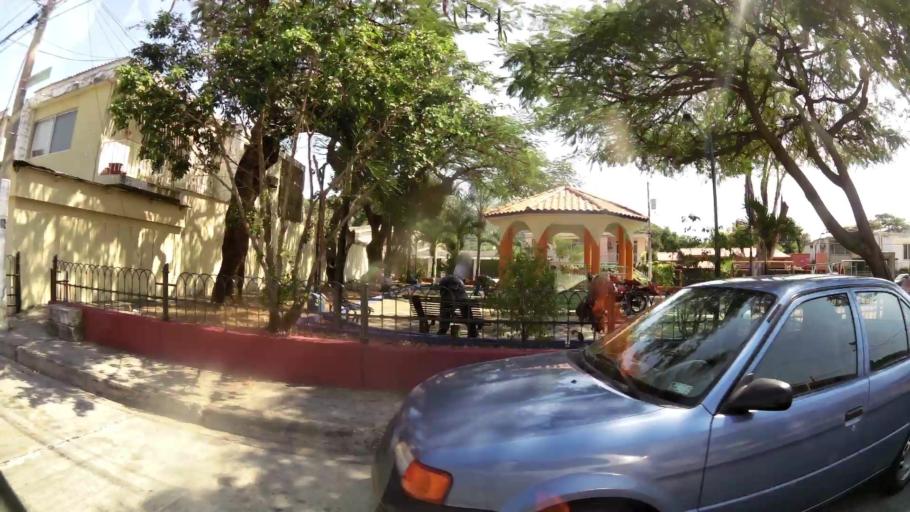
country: EC
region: Guayas
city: Guayaquil
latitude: -2.1679
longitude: -79.9139
